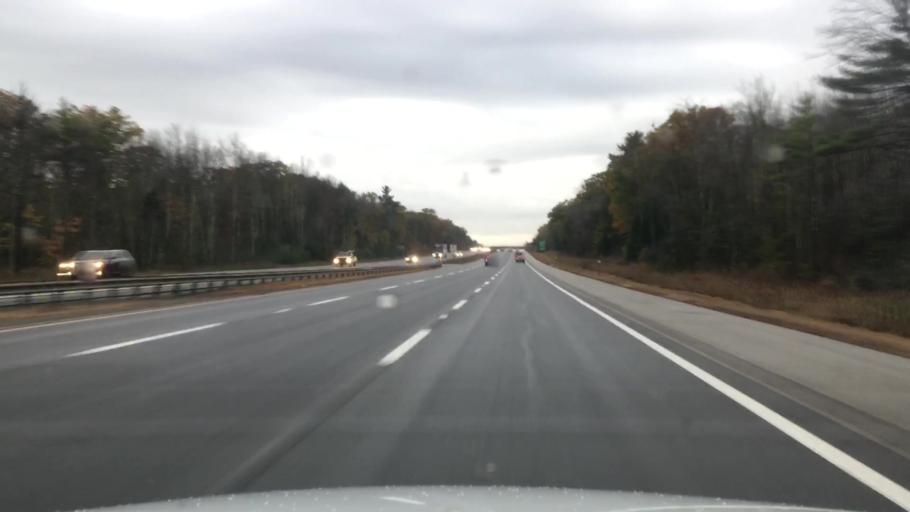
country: US
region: Maine
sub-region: York County
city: Wells Beach Station
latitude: 43.3404
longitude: -70.5988
